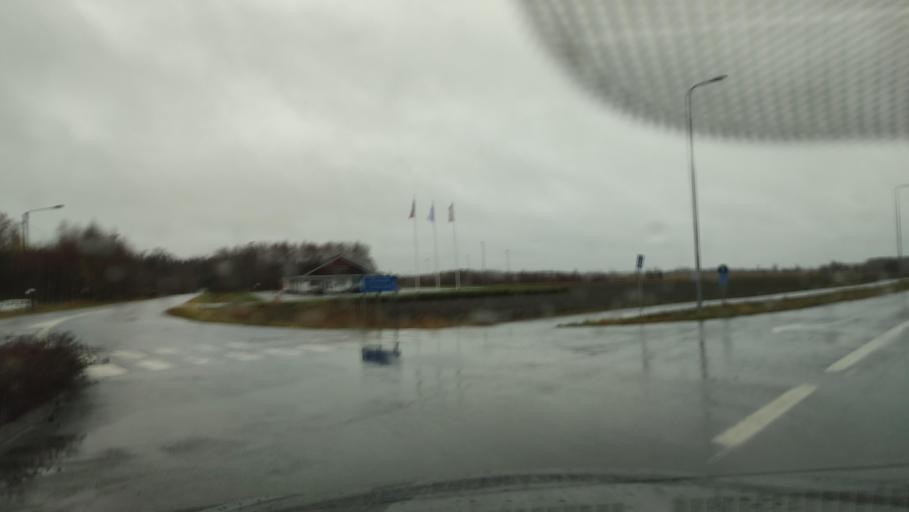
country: FI
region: Ostrobothnia
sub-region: Vaasa
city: Ristinummi
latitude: 63.0483
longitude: 21.7294
